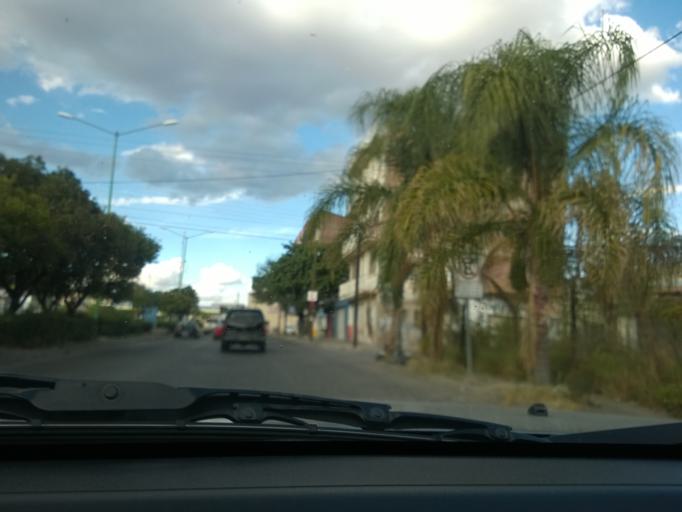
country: MX
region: Guanajuato
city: Leon
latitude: 21.1111
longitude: -101.6762
